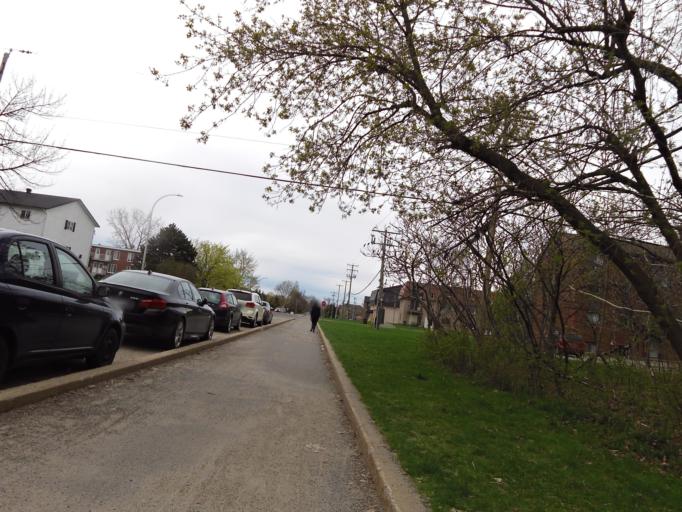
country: CA
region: Quebec
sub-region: Laurentides
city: Sainte-Marthe-sur-le-Lac
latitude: 45.5415
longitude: -73.9174
